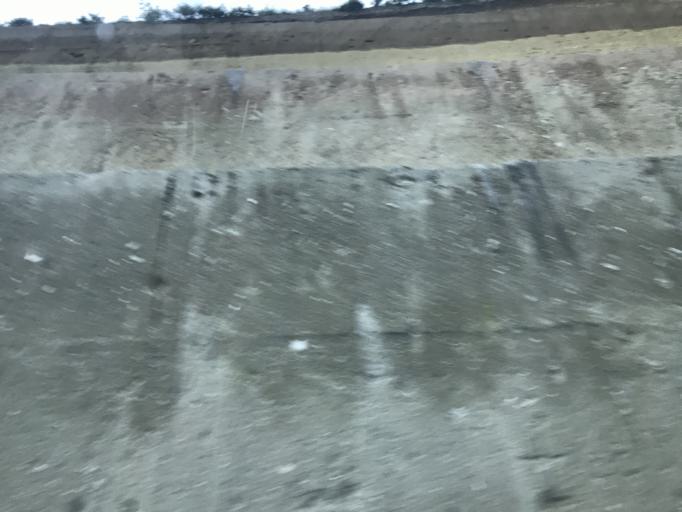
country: GT
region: Chimaltenango
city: El Tejar
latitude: 14.6371
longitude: -90.7936
